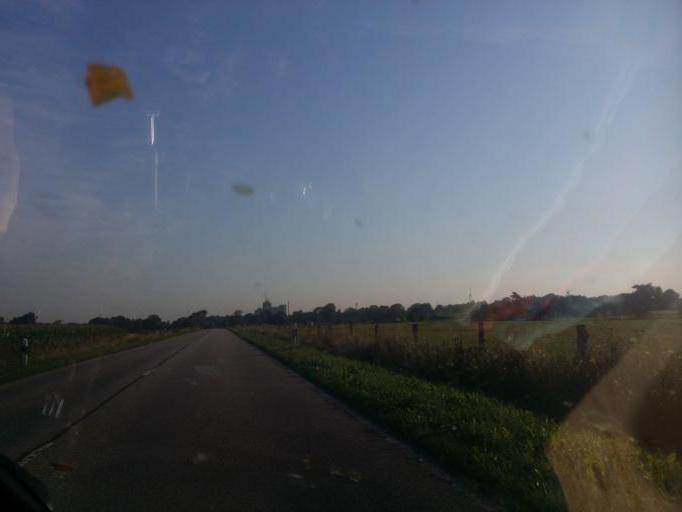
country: DE
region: Schleswig-Holstein
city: Suderlugum
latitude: 54.8635
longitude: 8.9034
